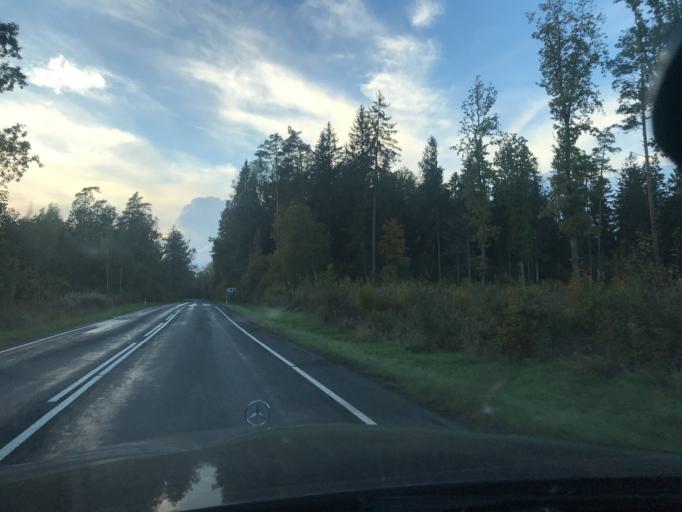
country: EE
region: Vorumaa
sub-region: Antsla vald
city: Vana-Antsla
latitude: 57.8818
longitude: 26.5712
